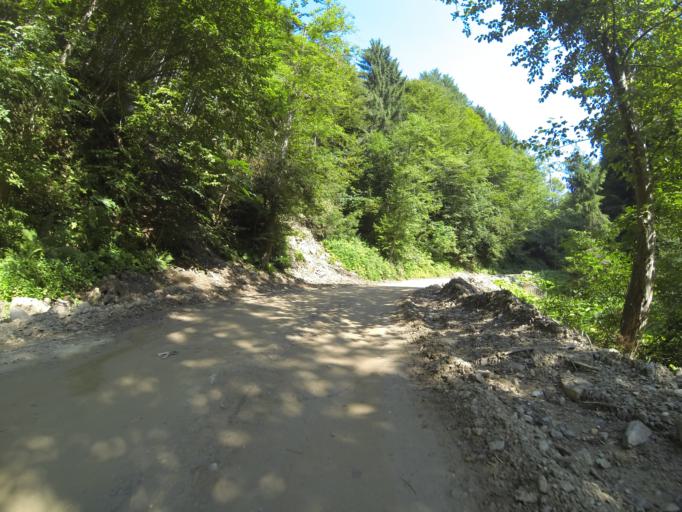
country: RO
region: Valcea
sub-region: Comuna Costesti
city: Bistrita
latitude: 45.2251
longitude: 24.0037
